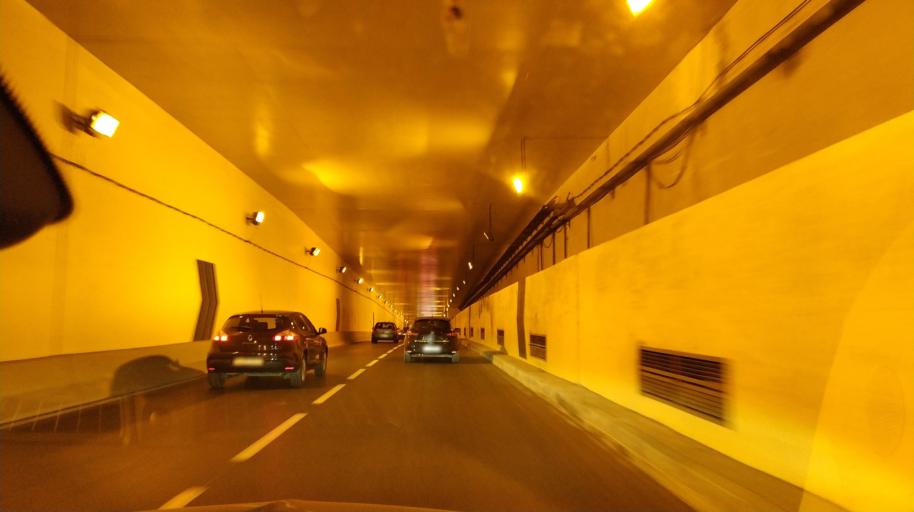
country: MA
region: Grand Casablanca
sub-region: Casablanca
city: Casablanca
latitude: 33.6075
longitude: -7.6312
